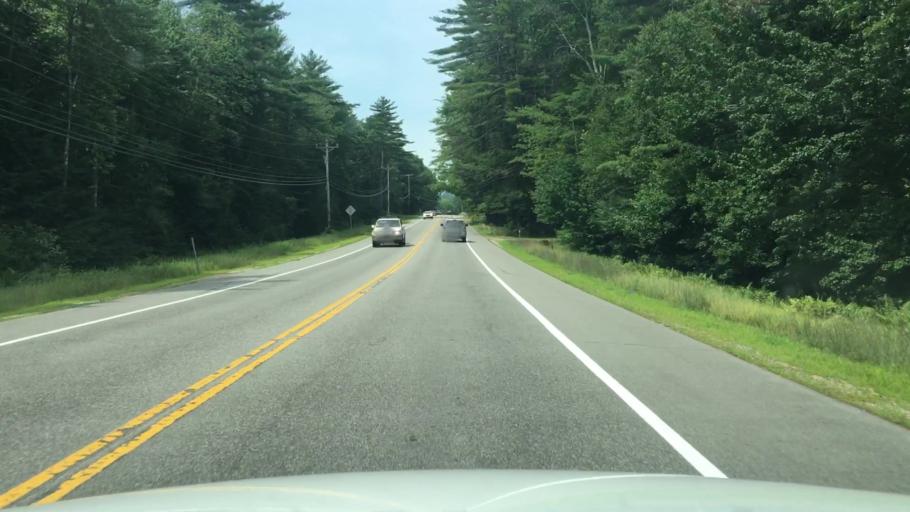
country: US
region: New Hampshire
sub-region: Belknap County
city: Meredith
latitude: 43.6214
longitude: -71.5647
